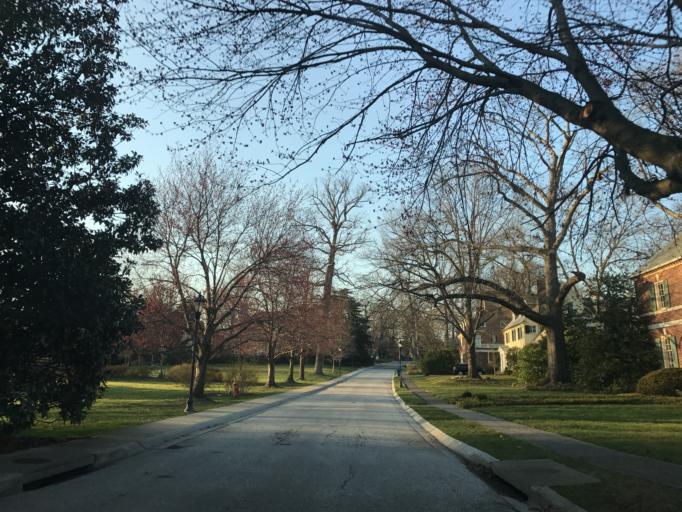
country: US
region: Maryland
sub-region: City of Baltimore
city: Baltimore
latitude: 39.3413
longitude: -76.6126
